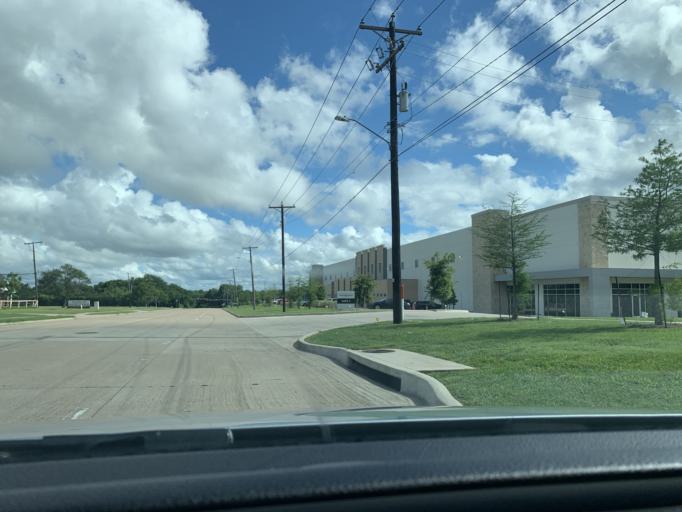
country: US
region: Texas
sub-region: Dallas County
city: Grand Prairie
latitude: 32.6725
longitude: -97.0310
